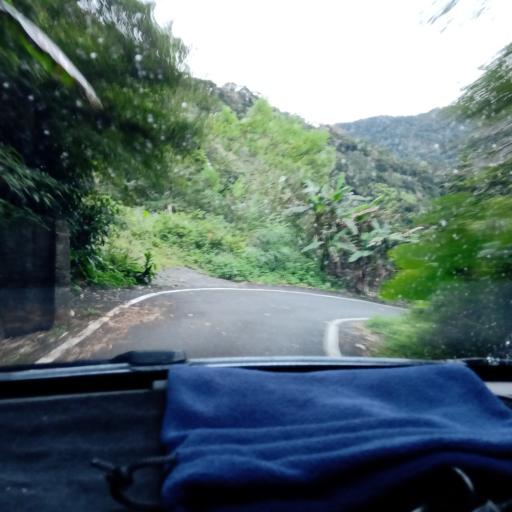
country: TW
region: Taiwan
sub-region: Yilan
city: Yilan
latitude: 24.8125
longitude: 121.7027
